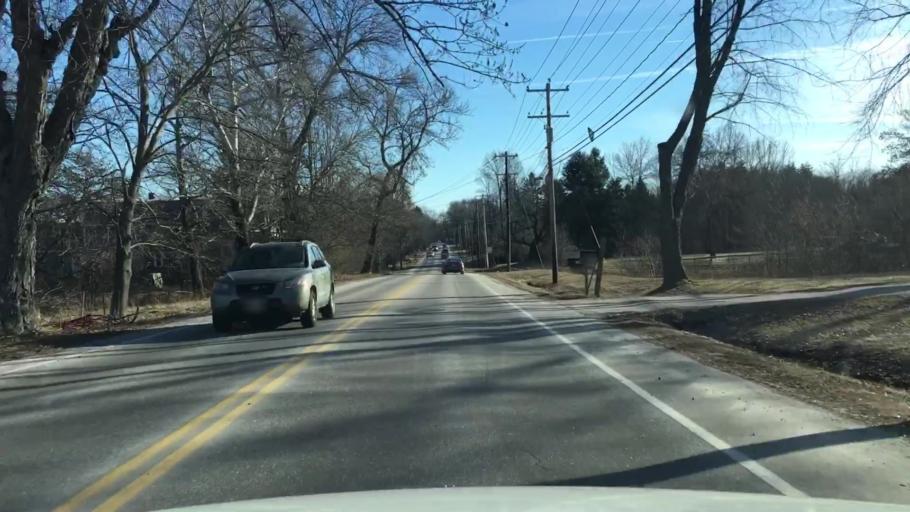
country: US
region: Maine
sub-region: Penobscot County
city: Bangor
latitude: 44.8176
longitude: -68.8006
